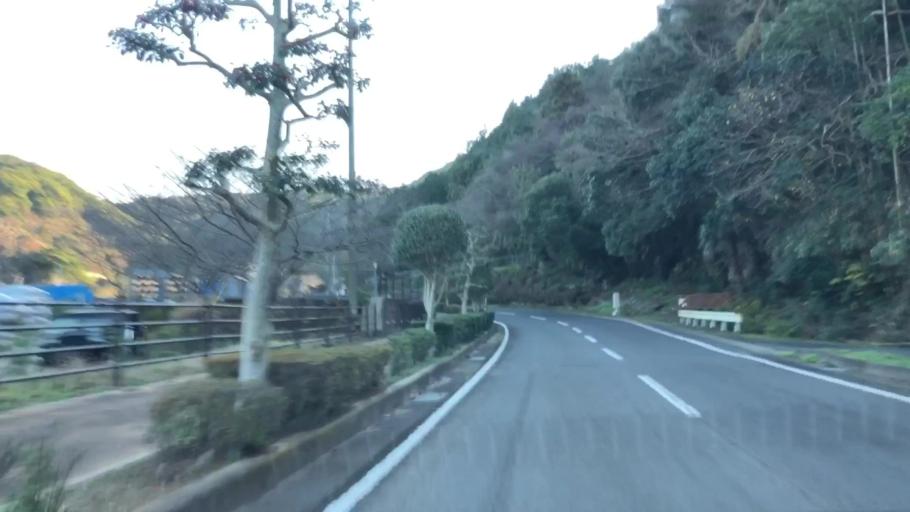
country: JP
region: Nagasaki
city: Sasebo
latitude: 33.0238
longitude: 129.6567
